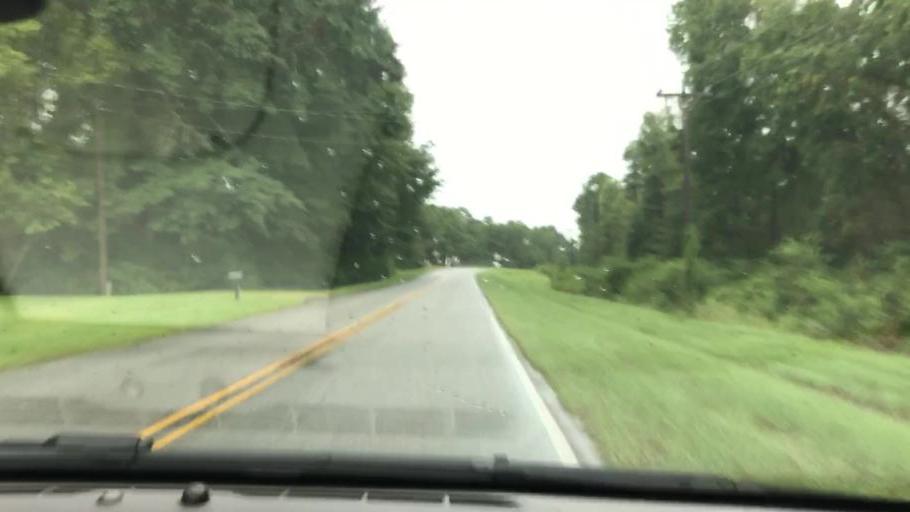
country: US
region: Georgia
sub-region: Clay County
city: Fort Gaines
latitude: 31.7210
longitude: -85.0438
